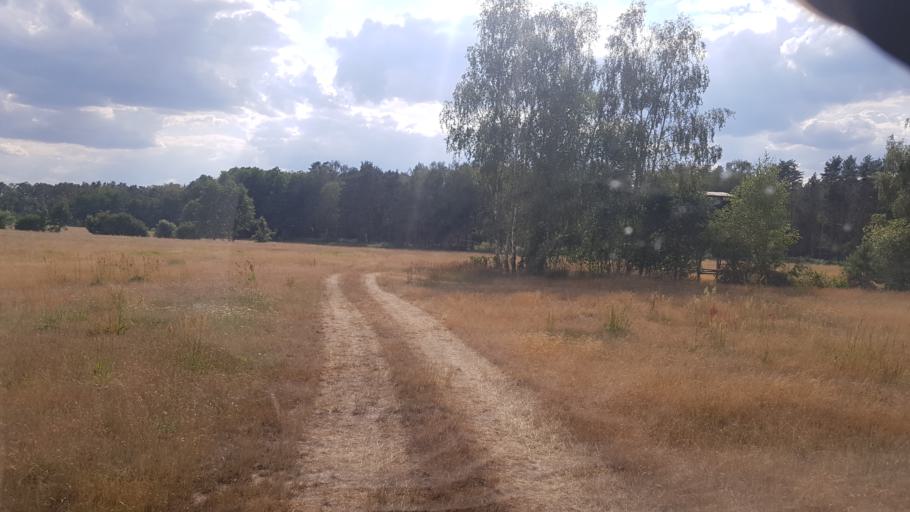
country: DE
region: Brandenburg
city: Schonborn
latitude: 51.5609
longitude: 13.4698
